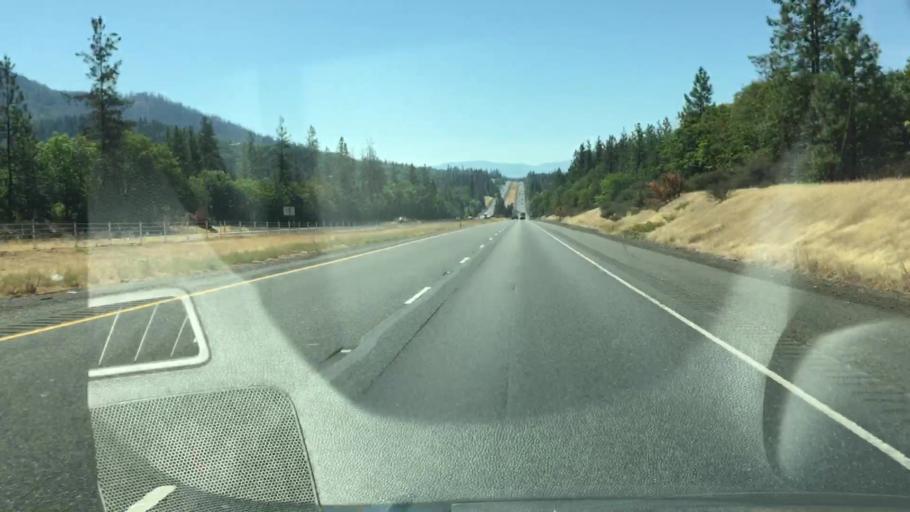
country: US
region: Oregon
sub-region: Josephine County
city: Merlin
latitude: 42.5662
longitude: -123.3725
